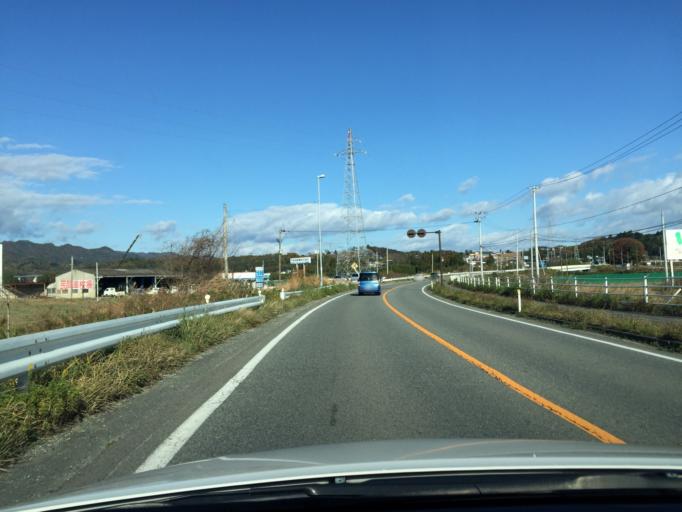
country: JP
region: Fukushima
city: Namie
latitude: 37.2720
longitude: 140.9932
